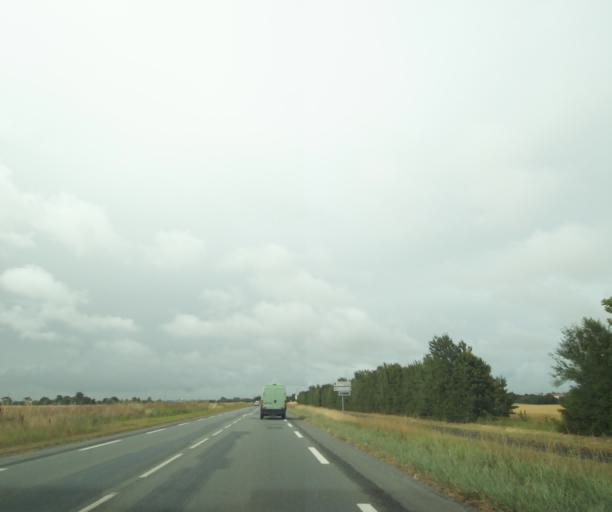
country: FR
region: Poitou-Charentes
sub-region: Departement de la Charente-Maritime
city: Lagord
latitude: 46.1953
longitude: -1.1407
